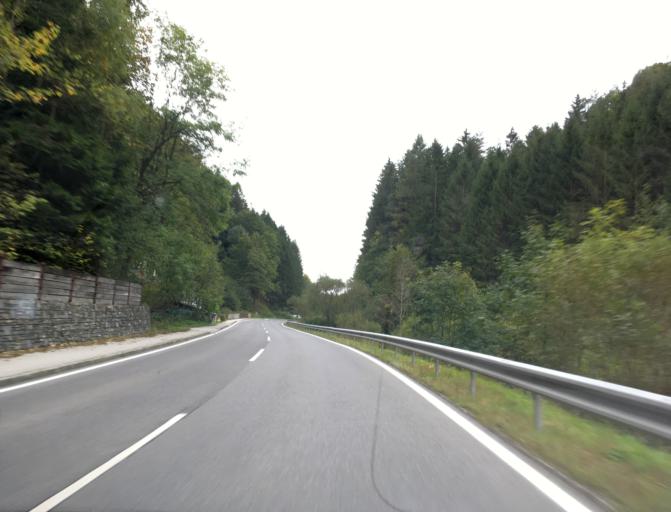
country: AT
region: Lower Austria
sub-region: Politischer Bezirk Neunkirchen
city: Edlitz
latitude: 47.5793
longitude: 16.1424
